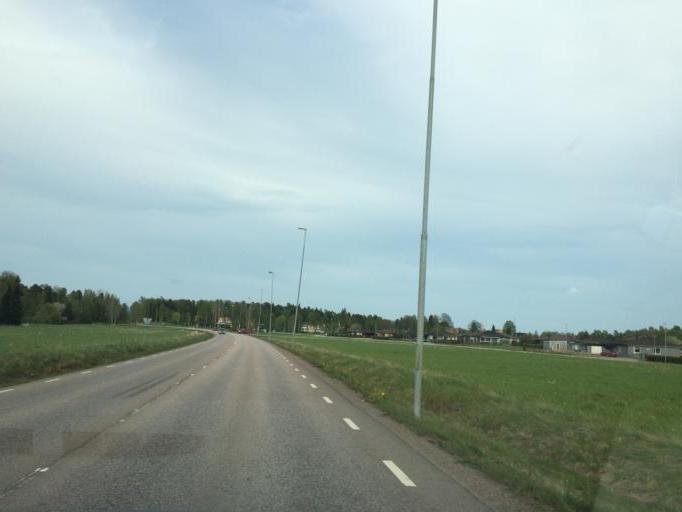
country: SE
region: Vaestmanland
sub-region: Hallstahammars Kommun
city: Hallstahammar
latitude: 59.6044
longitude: 16.2058
